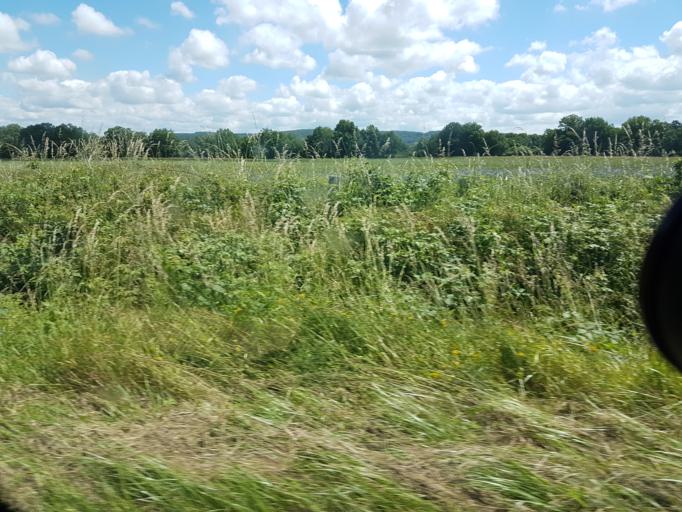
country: FR
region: Bourgogne
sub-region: Departement de Saone-et-Loire
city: Epinac
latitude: 46.9924
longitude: 4.4824
